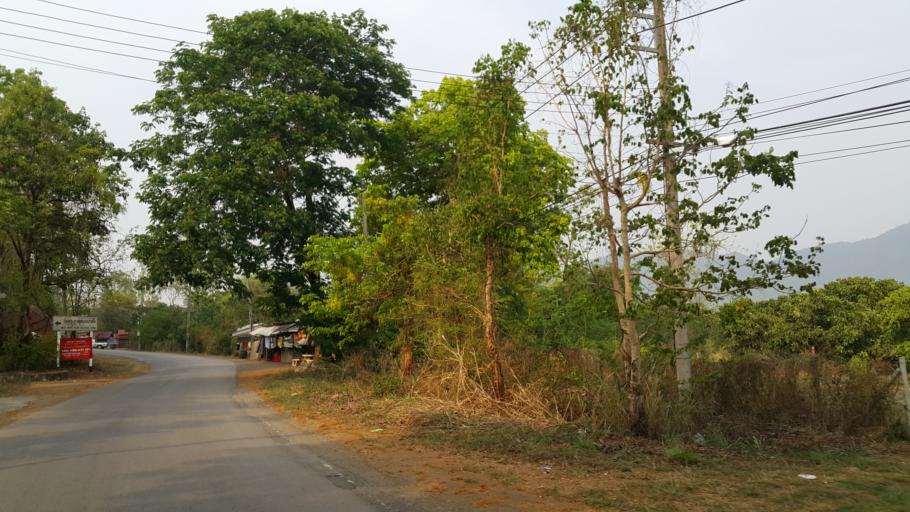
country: TH
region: Chiang Mai
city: Mae On
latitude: 18.7676
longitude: 99.2512
